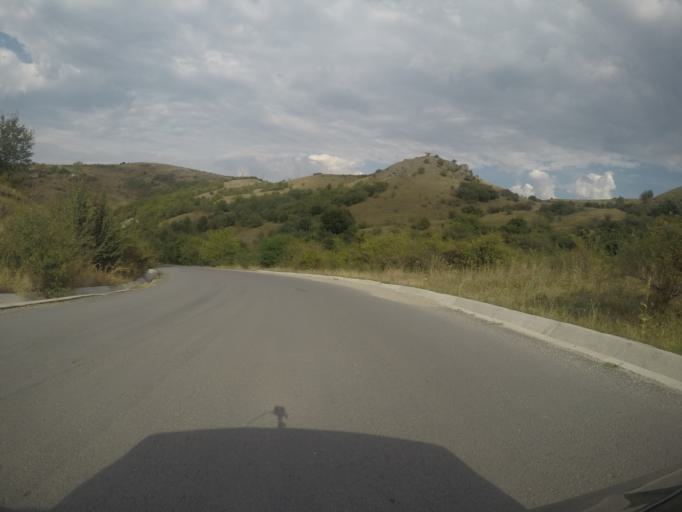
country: RO
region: Cluj
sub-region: Comuna Sandulesti
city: Sandulesti
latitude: 46.5581
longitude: 23.6941
